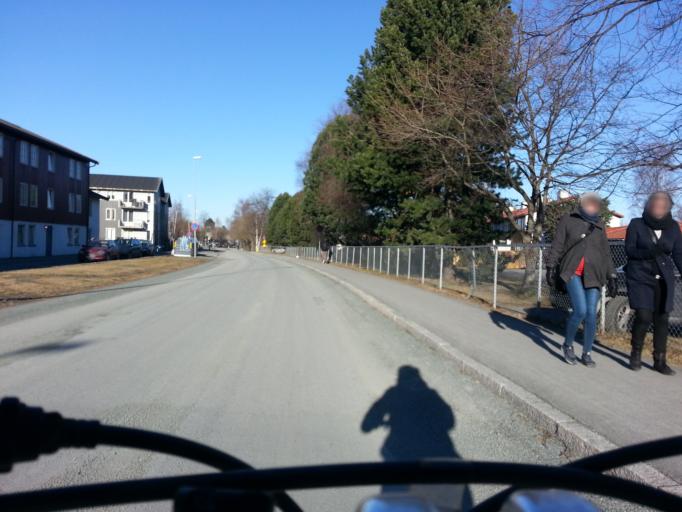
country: NO
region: Sor-Trondelag
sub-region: Trondheim
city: Trondheim
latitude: 63.4374
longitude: 10.4534
